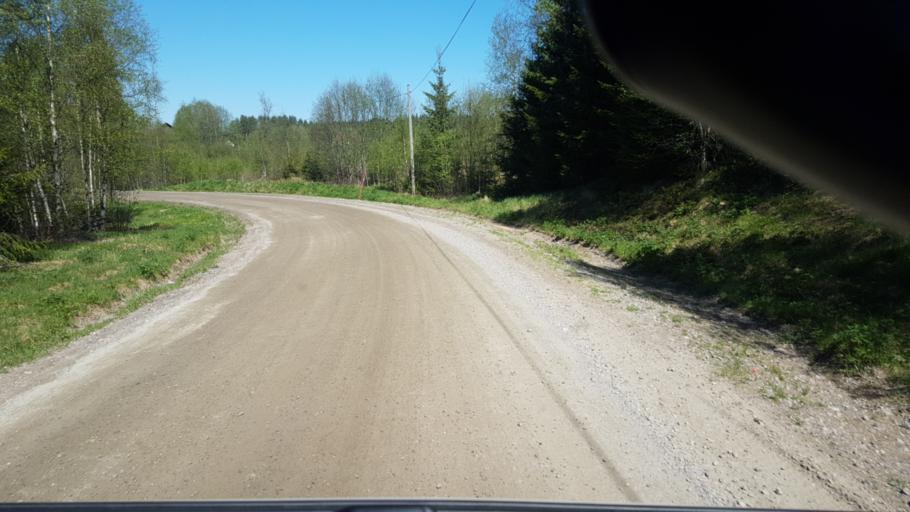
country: SE
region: Vaermland
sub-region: Arvika Kommun
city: Arvika
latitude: 59.8668
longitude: 12.6180
